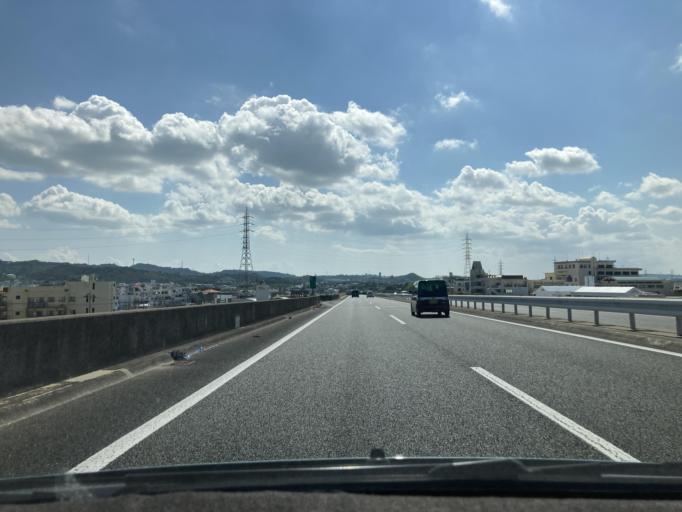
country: JP
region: Okinawa
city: Naha-shi
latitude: 26.2019
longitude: 127.7391
